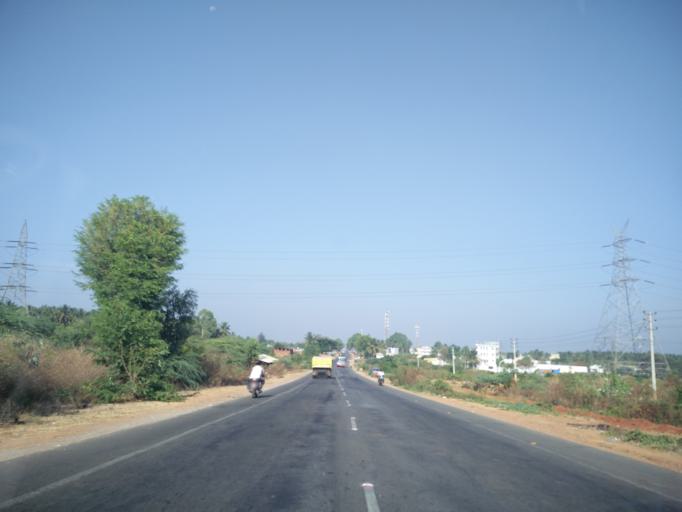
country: IN
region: Karnataka
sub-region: Tumkur
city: Tumkur
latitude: 13.3378
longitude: 77.0243
